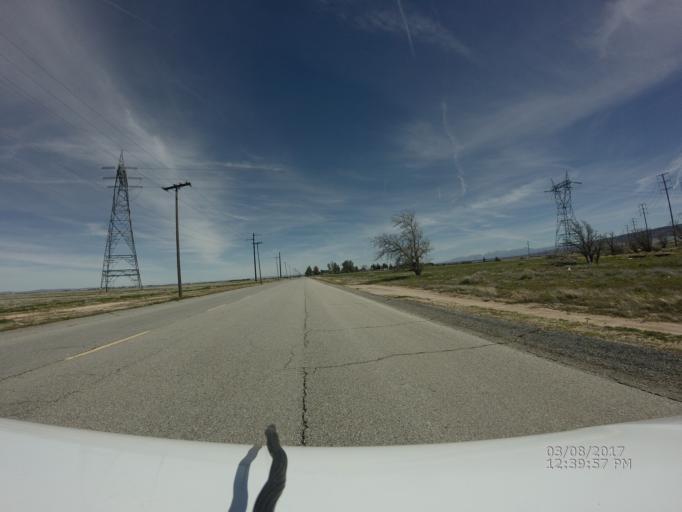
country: US
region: California
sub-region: Los Angeles County
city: Leona Valley
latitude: 34.7038
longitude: -118.3153
